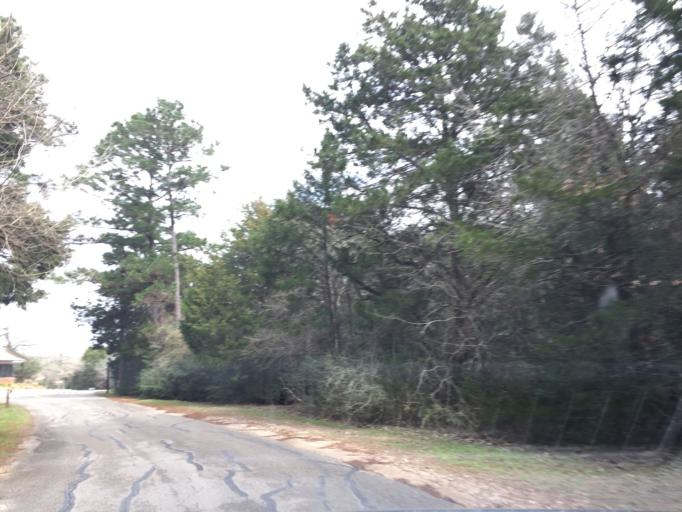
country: US
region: Texas
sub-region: Bastrop County
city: Bastrop
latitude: 30.1373
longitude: -97.2851
